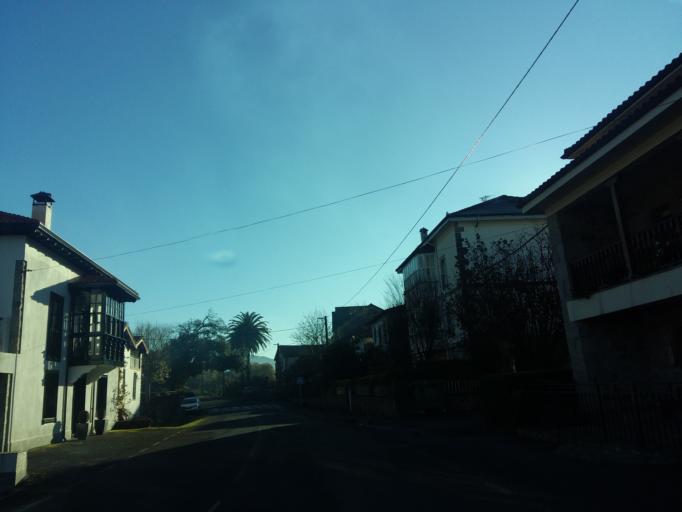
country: ES
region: Cantabria
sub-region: Provincia de Cantabria
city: Arredondo
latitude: 43.2812
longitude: -3.5383
